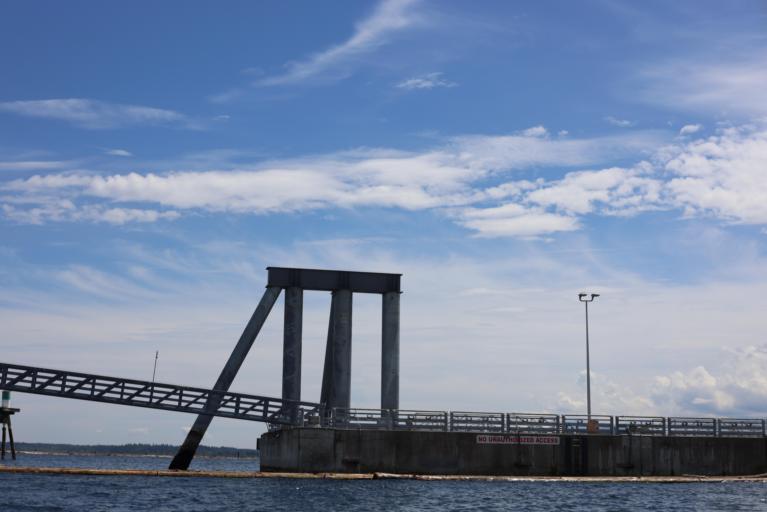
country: CA
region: British Columbia
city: Nanaimo
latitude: 49.1627
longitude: -123.9227
